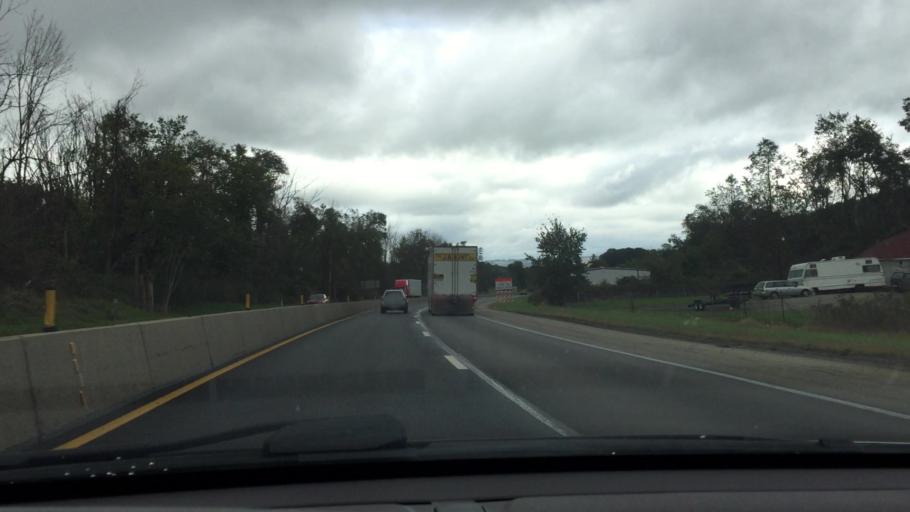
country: US
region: Pennsylvania
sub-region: Westmoreland County
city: Fellsburg
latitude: 40.1471
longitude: -79.8120
